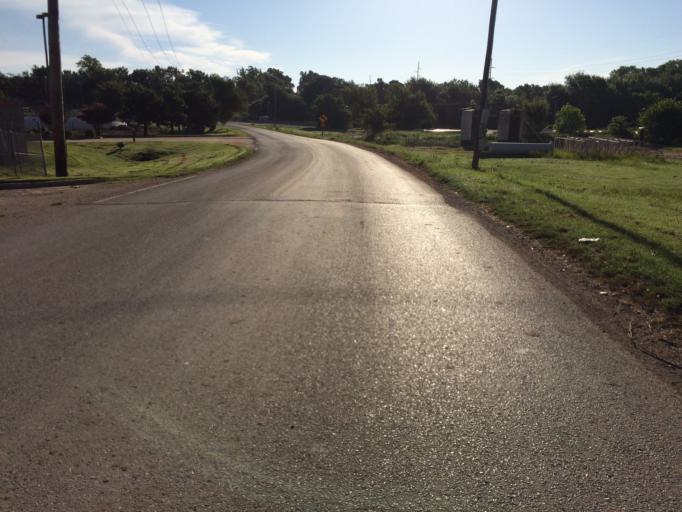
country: US
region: Oklahoma
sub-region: McClain County
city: Goldsby
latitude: 35.1742
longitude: -97.4432
